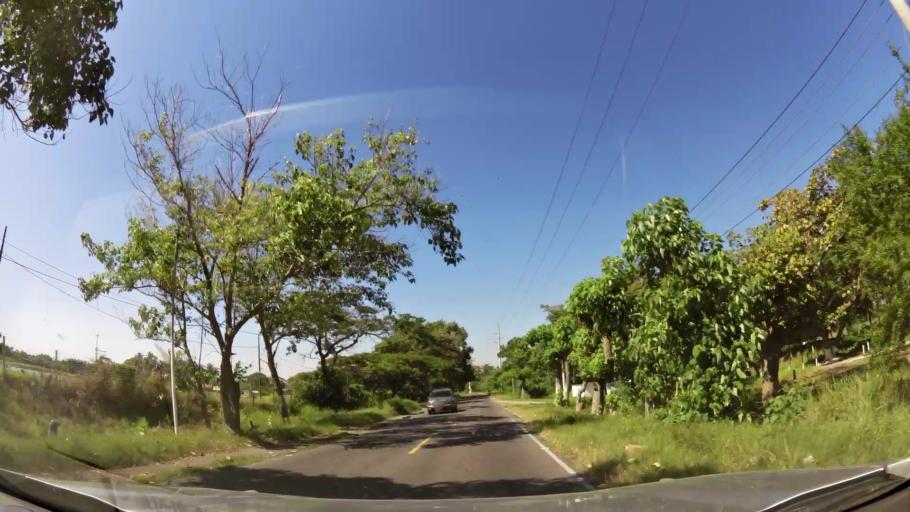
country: GT
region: Escuintla
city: Iztapa
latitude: 13.9373
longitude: -90.7409
